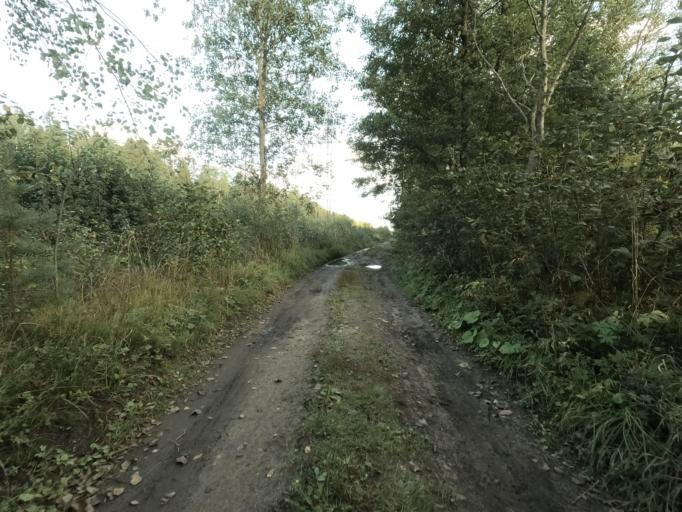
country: RU
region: Leningrad
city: Imeni Sverdlova
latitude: 59.8391
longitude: 30.7291
